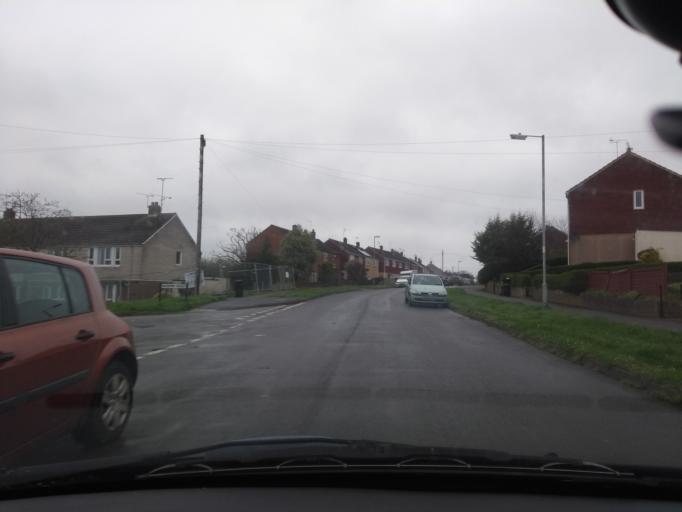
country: GB
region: England
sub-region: Somerset
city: Taunton
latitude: 51.0338
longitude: -3.0961
